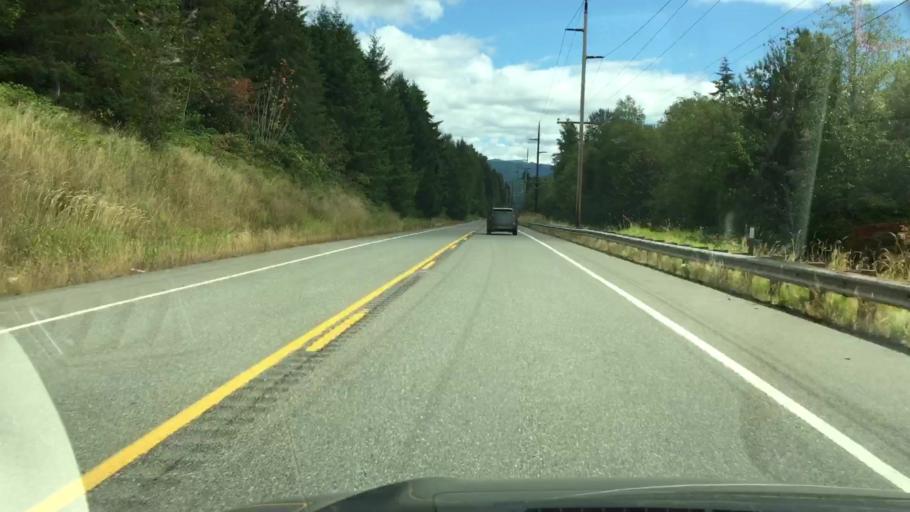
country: US
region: Washington
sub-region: Pierce County
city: Eatonville
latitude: 46.7765
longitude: -122.2241
